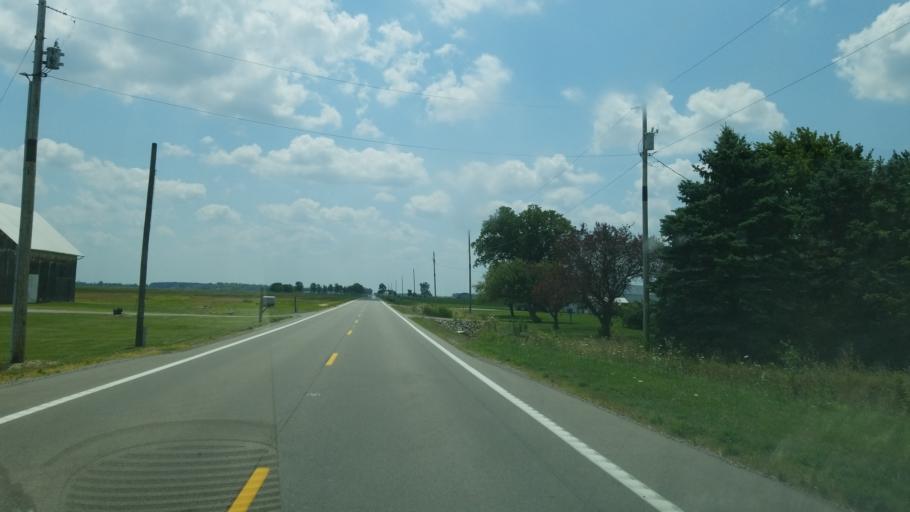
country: US
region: Ohio
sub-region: Henry County
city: Deshler
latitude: 41.2960
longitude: -83.9410
